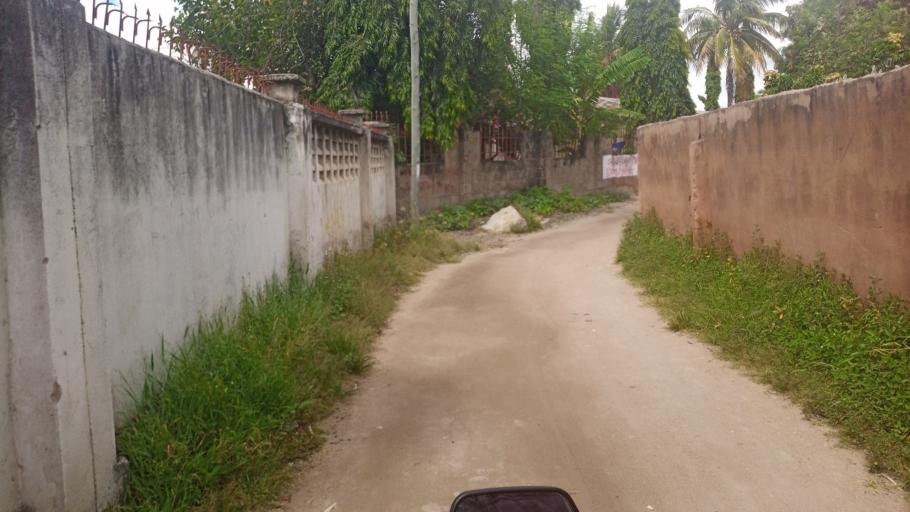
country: TZ
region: Dodoma
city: Dodoma
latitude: -6.1909
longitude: 35.7347
